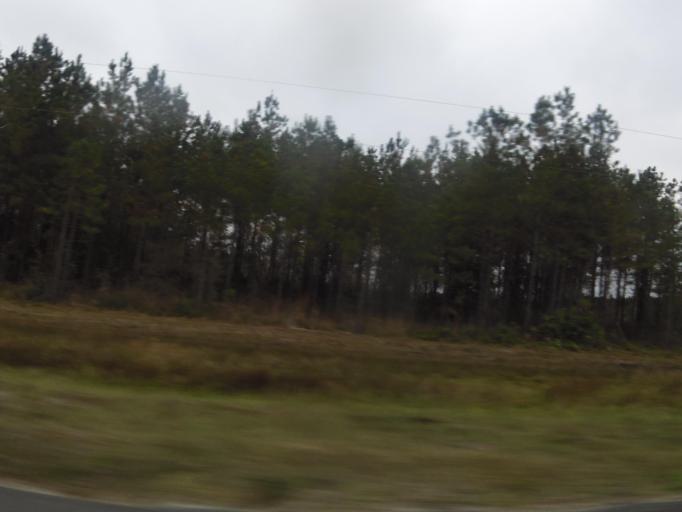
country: US
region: Georgia
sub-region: Charlton County
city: Folkston
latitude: 30.8859
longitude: -82.0421
